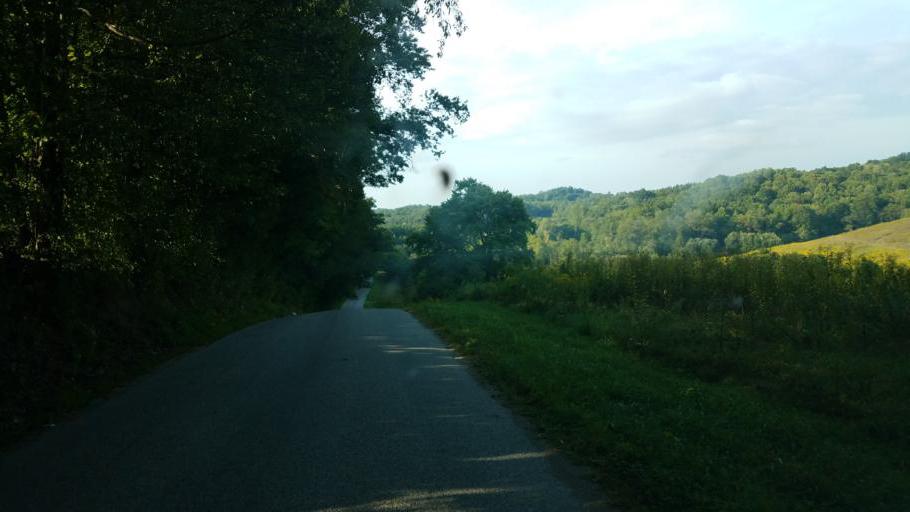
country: US
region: Ohio
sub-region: Sandusky County
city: Bellville
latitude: 40.6188
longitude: -82.4813
